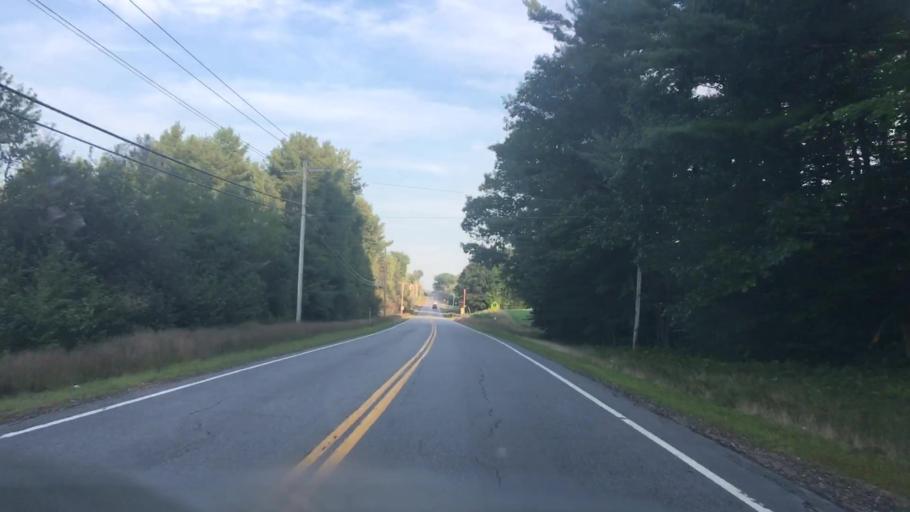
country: US
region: New Hampshire
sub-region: Belknap County
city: Gilmanton
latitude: 43.4260
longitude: -71.3364
